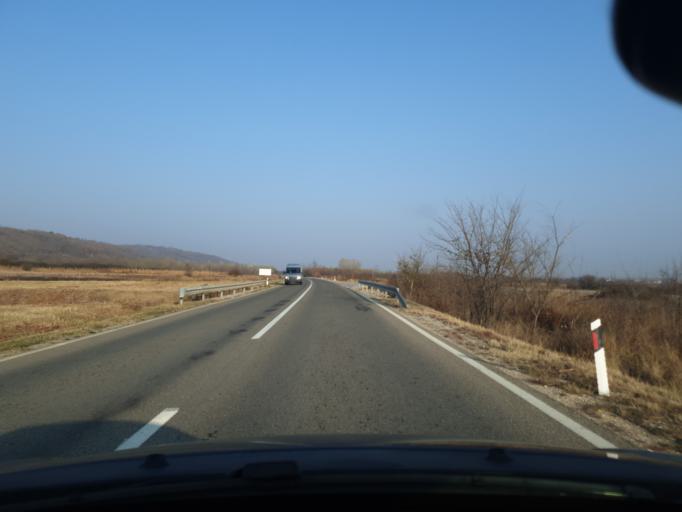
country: RS
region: Central Serbia
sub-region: Jablanicki Okrug
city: Leskovac
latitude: 42.9527
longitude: 21.9896
